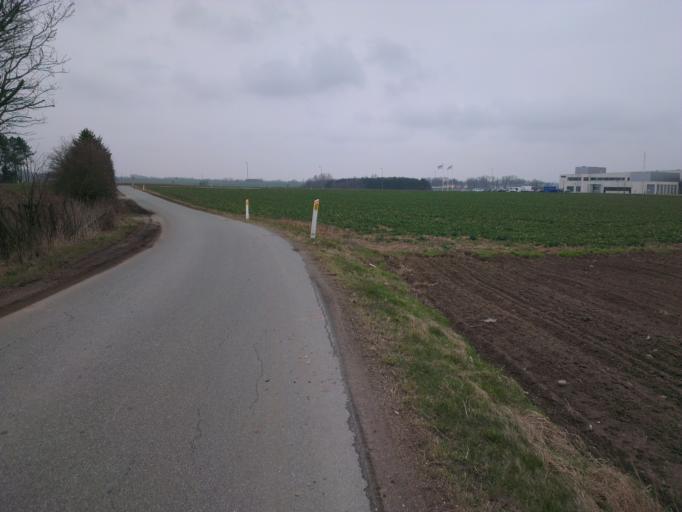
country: DK
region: Capital Region
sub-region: Frederikssund Kommune
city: Frederikssund
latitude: 55.8249
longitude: 12.1111
